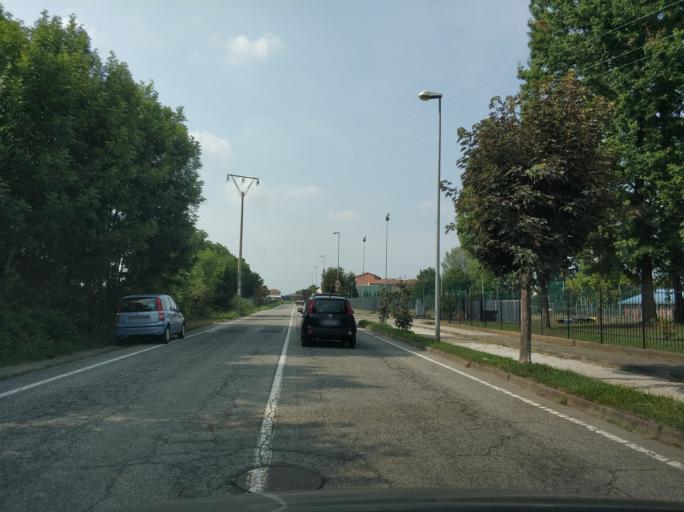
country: IT
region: Piedmont
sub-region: Provincia di Torino
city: Leini
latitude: 45.1752
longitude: 7.7101
